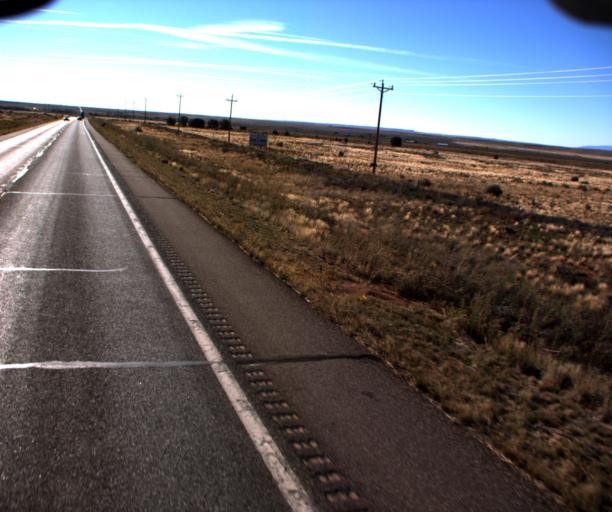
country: US
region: Arizona
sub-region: Mohave County
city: Colorado City
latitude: 36.9512
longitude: -112.9596
